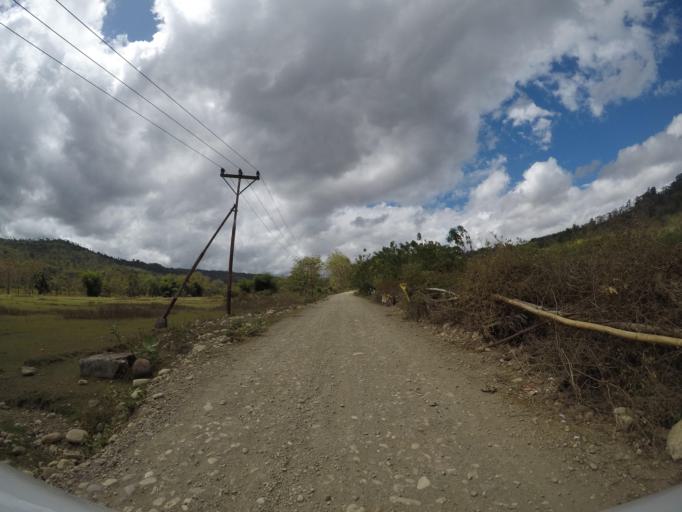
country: TL
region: Lautem
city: Lospalos
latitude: -8.4951
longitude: 126.8244
